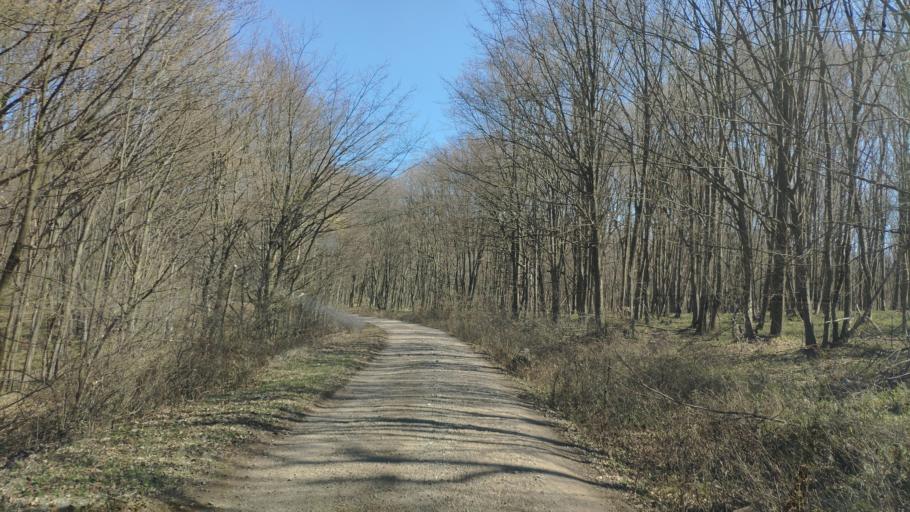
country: SK
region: Kosicky
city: Roznava
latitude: 48.5948
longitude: 20.4106
